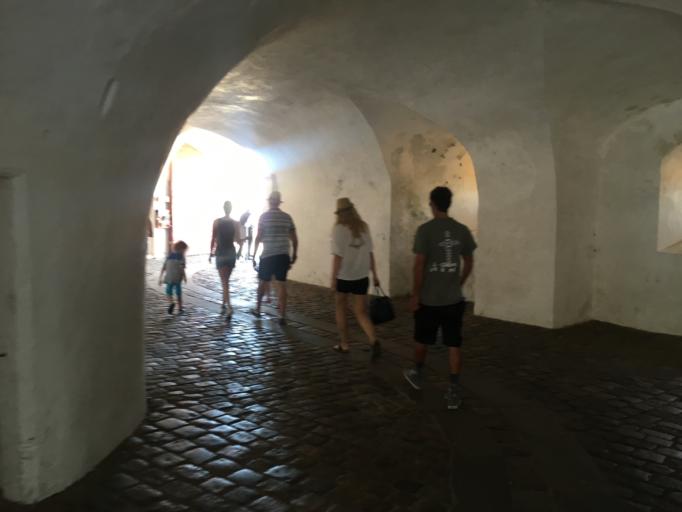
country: DK
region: Capital Region
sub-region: Helsingor Kommune
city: Helsingor
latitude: 56.0395
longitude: 12.6217
